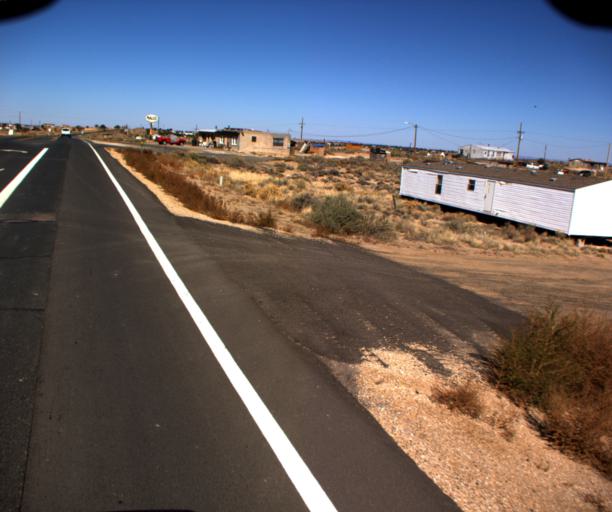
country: US
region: Arizona
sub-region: Navajo County
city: First Mesa
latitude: 35.8163
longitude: -110.5297
